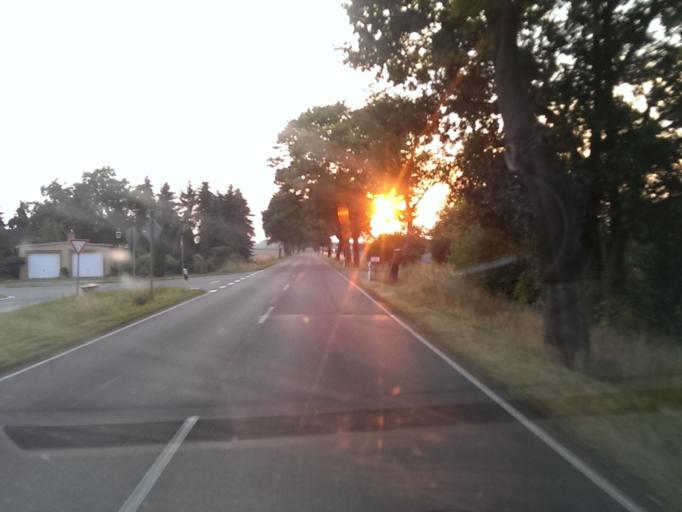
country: DE
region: Brandenburg
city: Golssen
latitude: 51.9759
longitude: 13.5950
